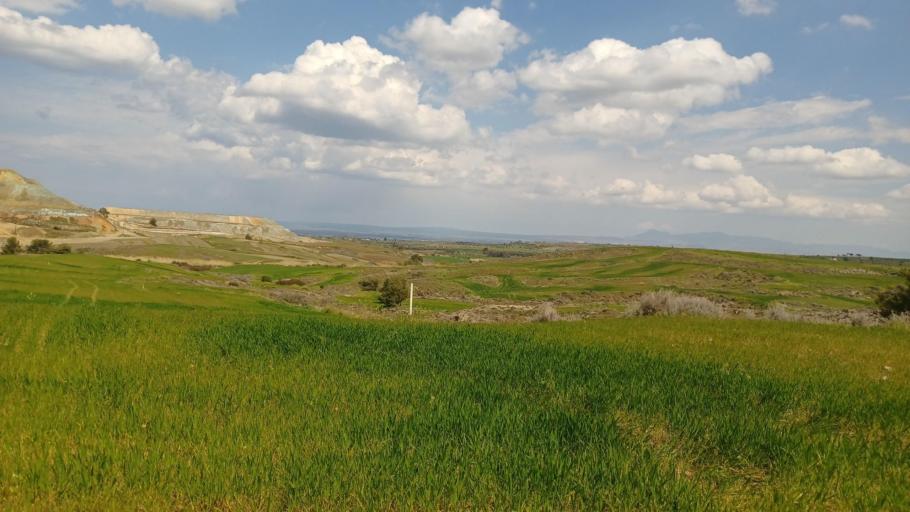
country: CY
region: Lefkosia
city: Lefka
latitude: 35.0822
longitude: 32.9047
